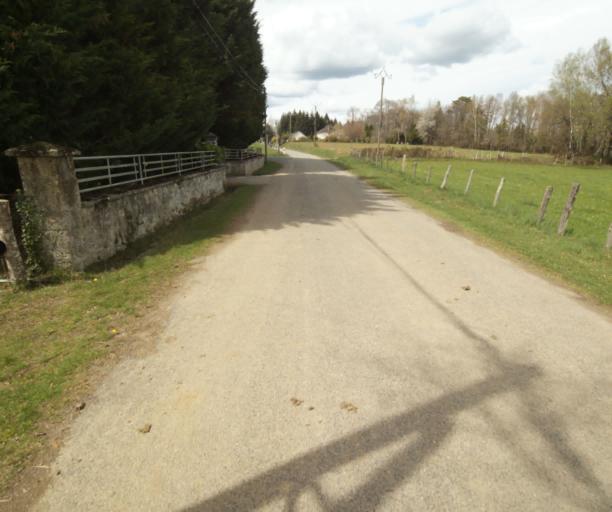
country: FR
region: Limousin
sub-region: Departement de la Correze
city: Laguenne
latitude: 45.2273
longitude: 1.8793
